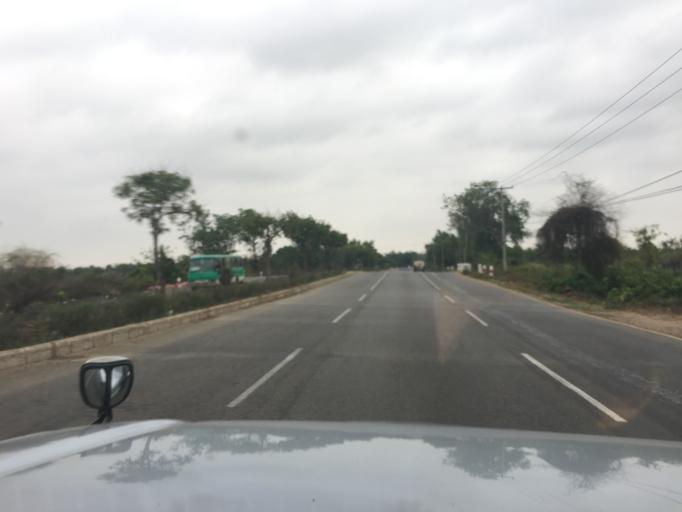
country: MM
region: Bago
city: Bago
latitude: 17.2302
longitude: 96.4573
